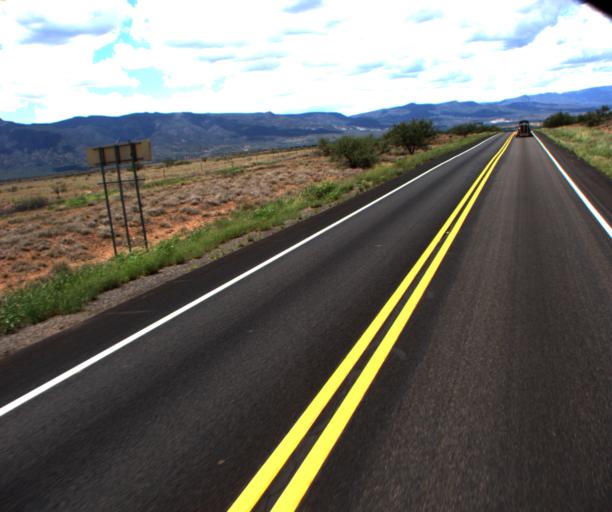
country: US
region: Arizona
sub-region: Yavapai County
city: Camp Verde
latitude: 34.5065
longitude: -111.7638
